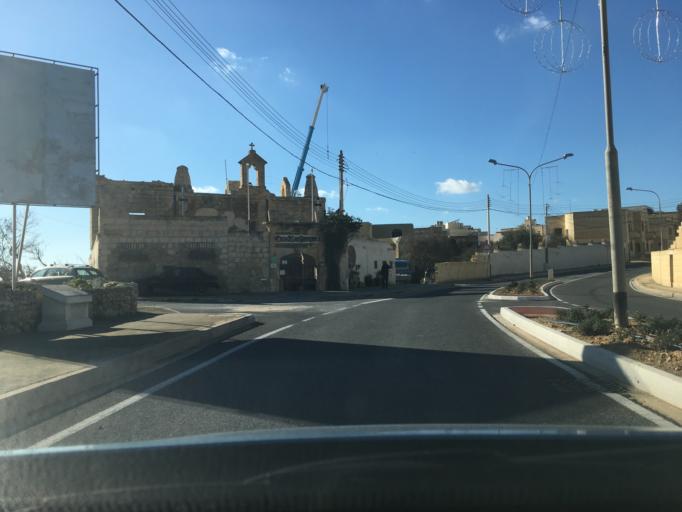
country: MT
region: Ghajnsielem
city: Ghajnsielem
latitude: 36.0237
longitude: 14.2896
